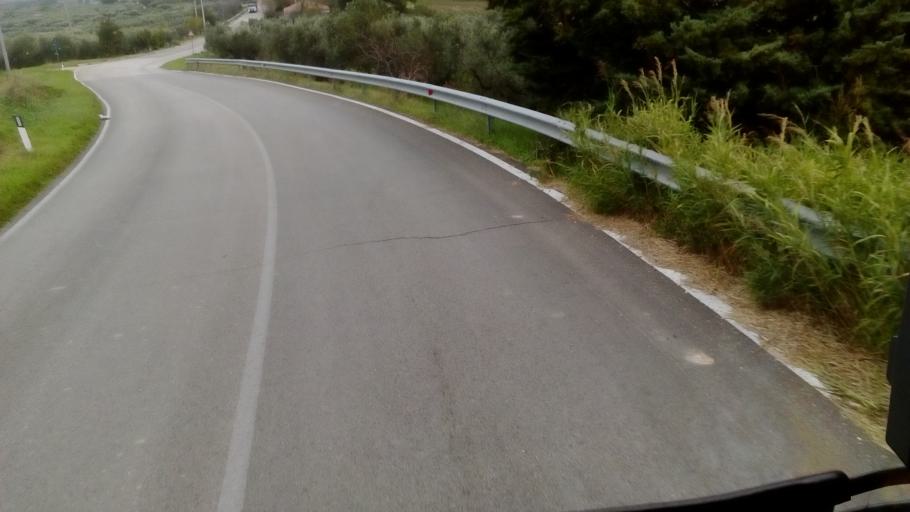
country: IT
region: Abruzzo
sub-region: Provincia di Chieti
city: Cupello
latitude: 42.0594
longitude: 14.6946
